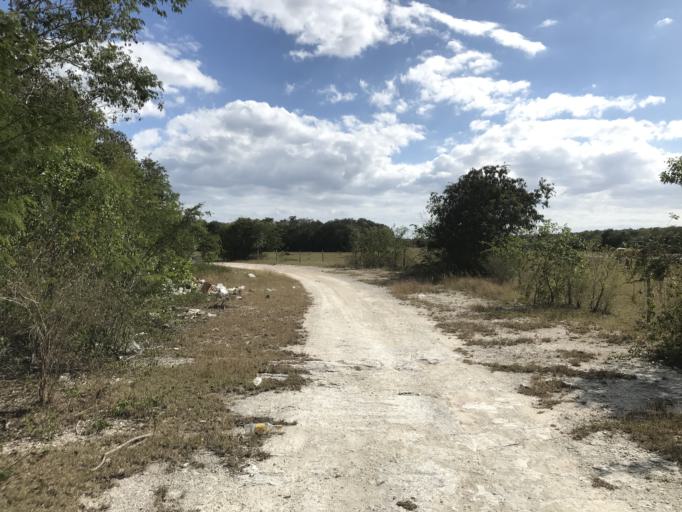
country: CU
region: Cienfuegos
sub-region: Municipio de Aguada de Pasajeros
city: Aguada de Pasajeros
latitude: 22.0763
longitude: -81.0382
